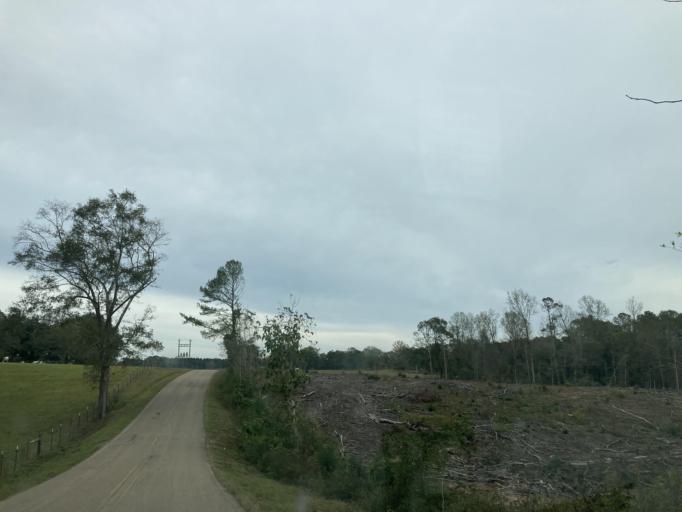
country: US
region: Mississippi
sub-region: Lamar County
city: Lumberton
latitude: 31.0412
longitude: -89.4533
